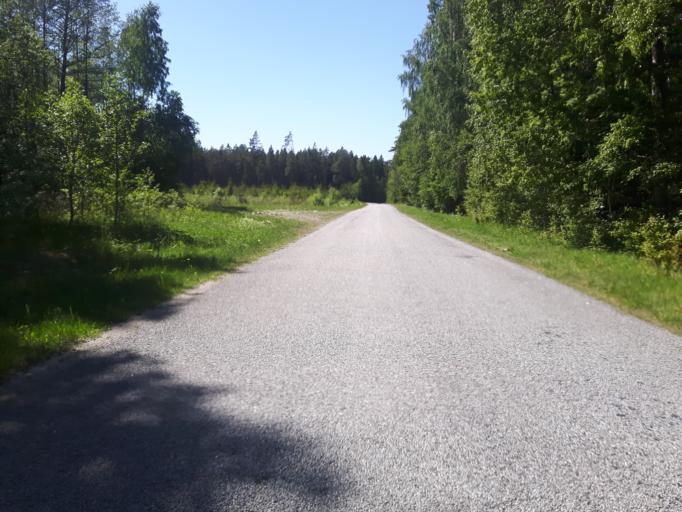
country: EE
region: Laeaene-Virumaa
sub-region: Haljala vald
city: Haljala
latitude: 59.5524
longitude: 26.3547
